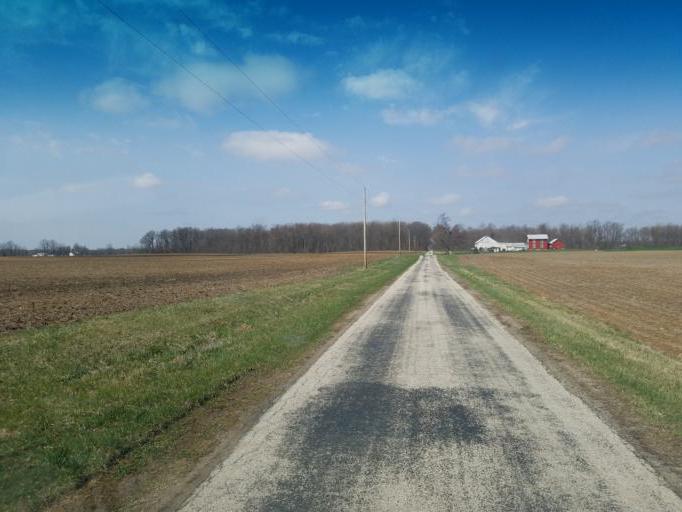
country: US
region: Ohio
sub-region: Crawford County
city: Bucyrus
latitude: 40.9356
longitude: -83.0776
